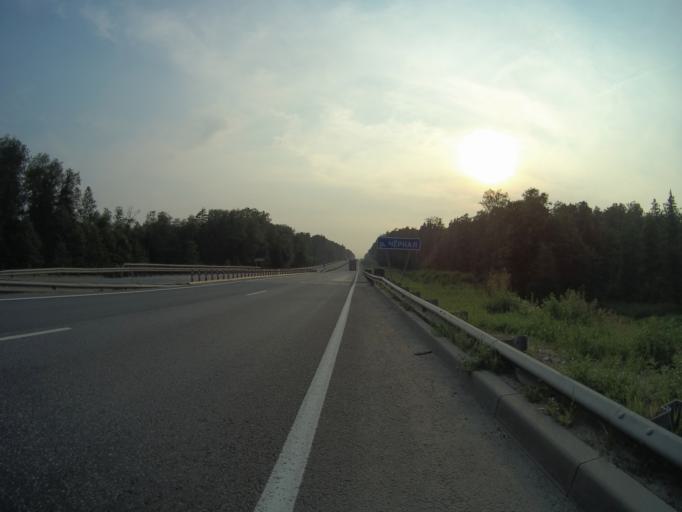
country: RU
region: Vladimir
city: Kameshkovo
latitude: 56.1971
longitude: 41.0075
